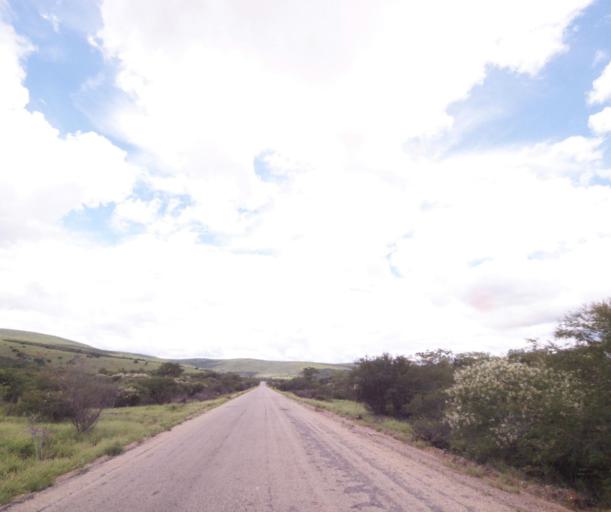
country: BR
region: Bahia
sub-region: Brumado
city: Brumado
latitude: -14.1877
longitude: -41.5750
